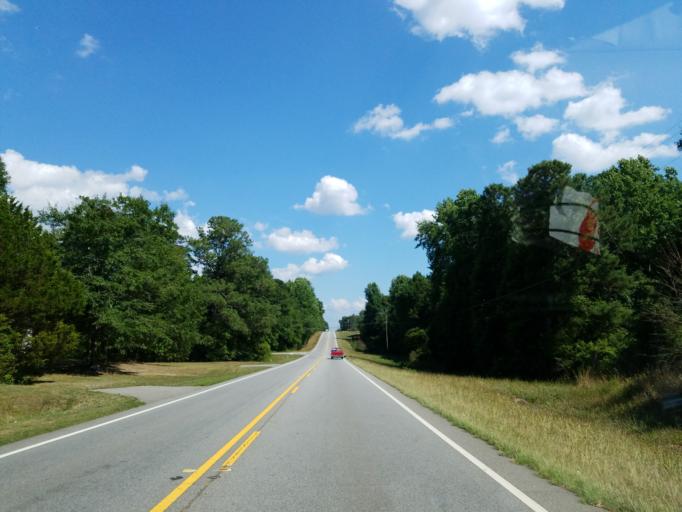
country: US
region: Georgia
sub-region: Lamar County
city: Barnesville
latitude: 33.0257
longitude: -84.1403
